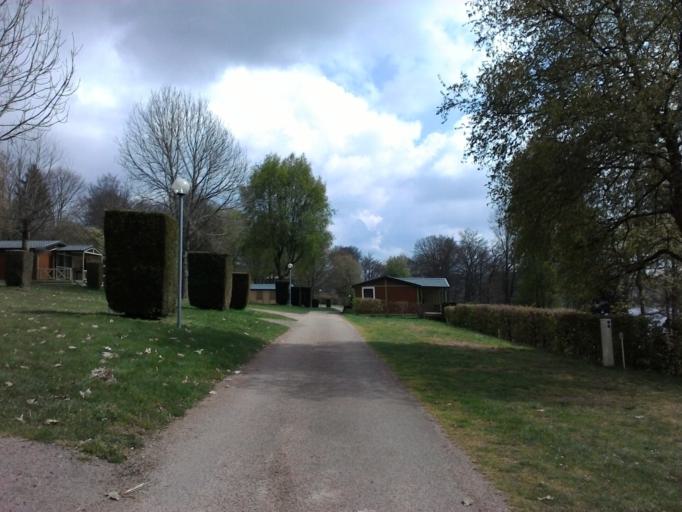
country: FR
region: Bourgogne
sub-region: Departement de la Nievre
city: Chateau-Chinon(Ville)
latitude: 47.1850
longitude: 4.0717
